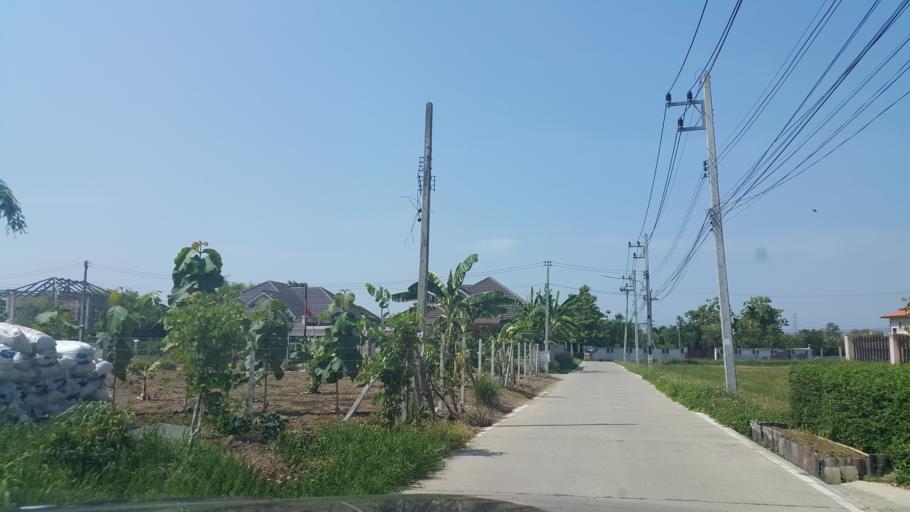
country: TH
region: Chiang Mai
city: Saraphi
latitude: 18.7263
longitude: 98.9731
